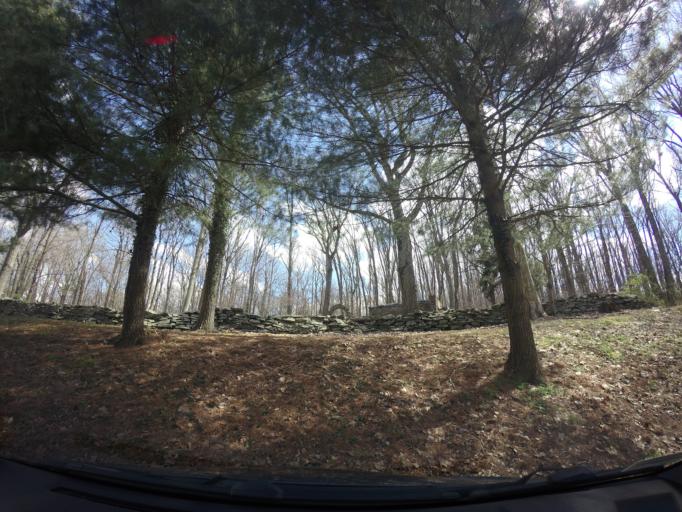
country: US
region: Maryland
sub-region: Frederick County
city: Brunswick
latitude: 39.4046
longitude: -77.6404
